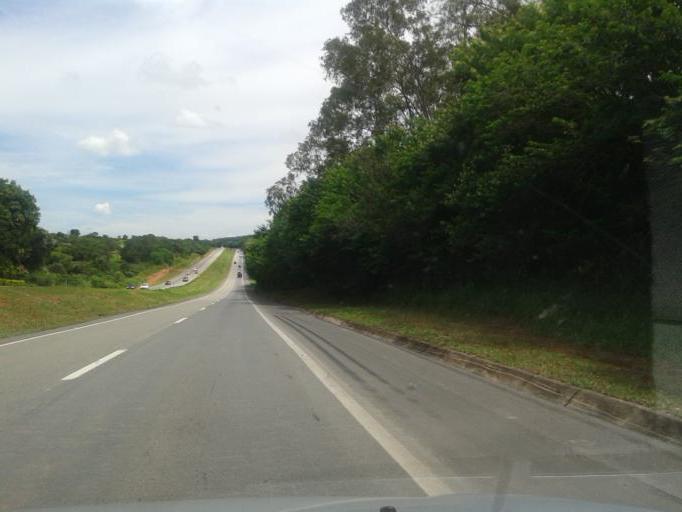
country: BR
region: Goias
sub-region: Hidrolandia
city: Hidrolandia
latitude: -17.1035
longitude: -49.2176
